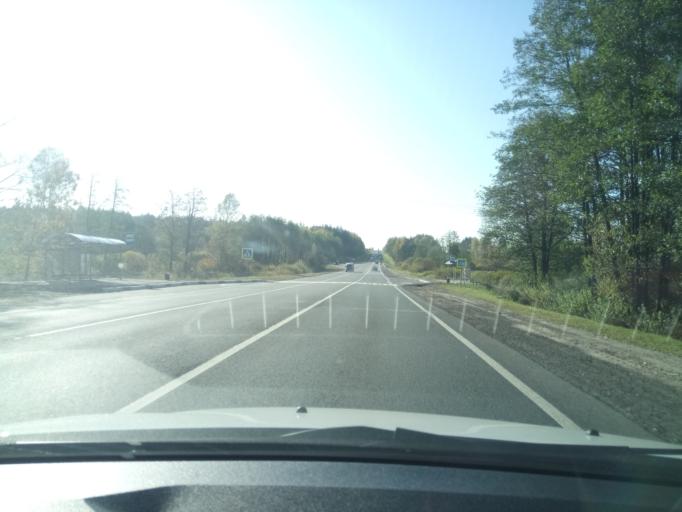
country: RU
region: Nizjnij Novgorod
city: Dal'neye Konstantinovo
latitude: 55.9826
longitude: 43.9712
